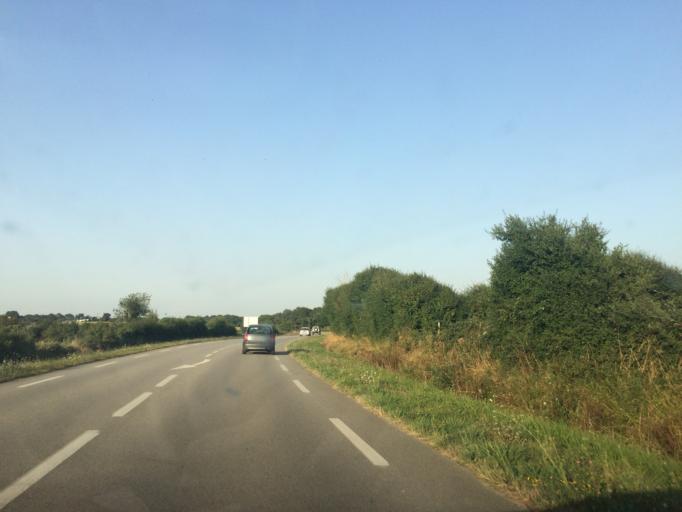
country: FR
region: Brittany
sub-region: Departement du Morbihan
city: Ambon
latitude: 47.5372
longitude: -2.5412
